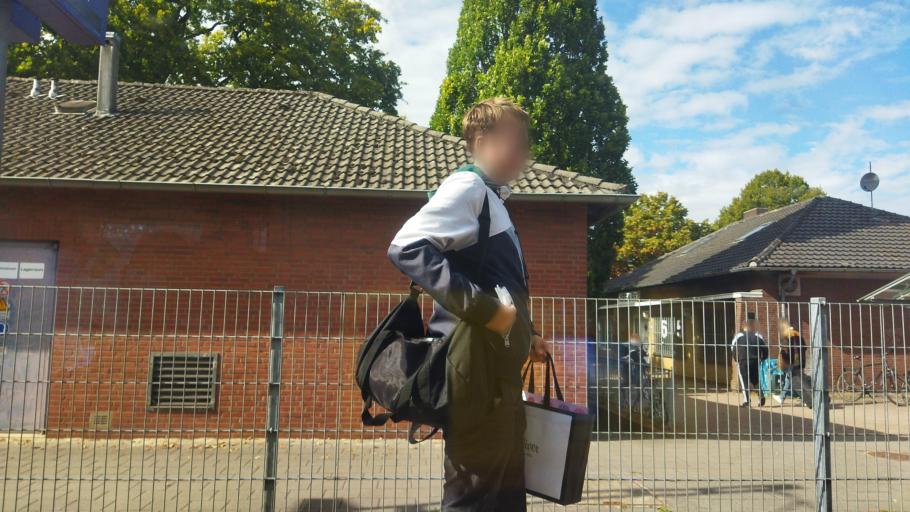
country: DE
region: Lower Saxony
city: Haren
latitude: 52.7853
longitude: 7.3014
